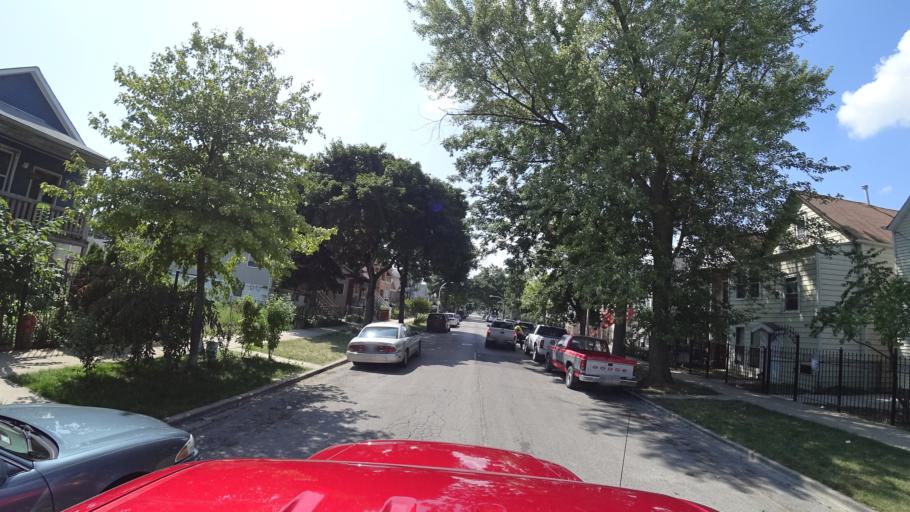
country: US
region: Illinois
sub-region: Cook County
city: Chicago
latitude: 41.8192
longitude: -87.6884
